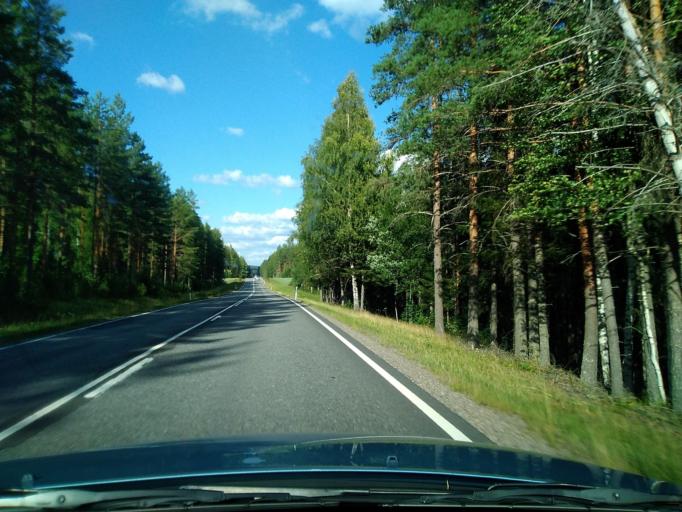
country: FI
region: Pirkanmaa
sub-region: Ylae-Pirkanmaa
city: Maenttae
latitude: 61.9630
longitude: 24.5919
